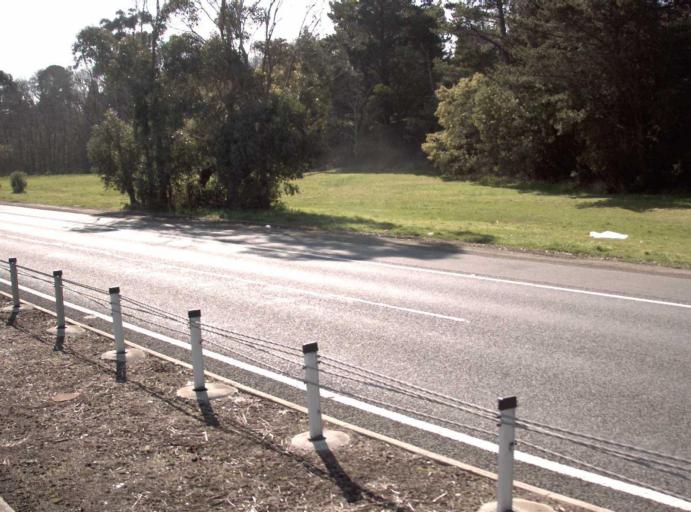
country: AU
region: Tasmania
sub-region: Launceston
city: Newnham
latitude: -41.4033
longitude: 147.1197
